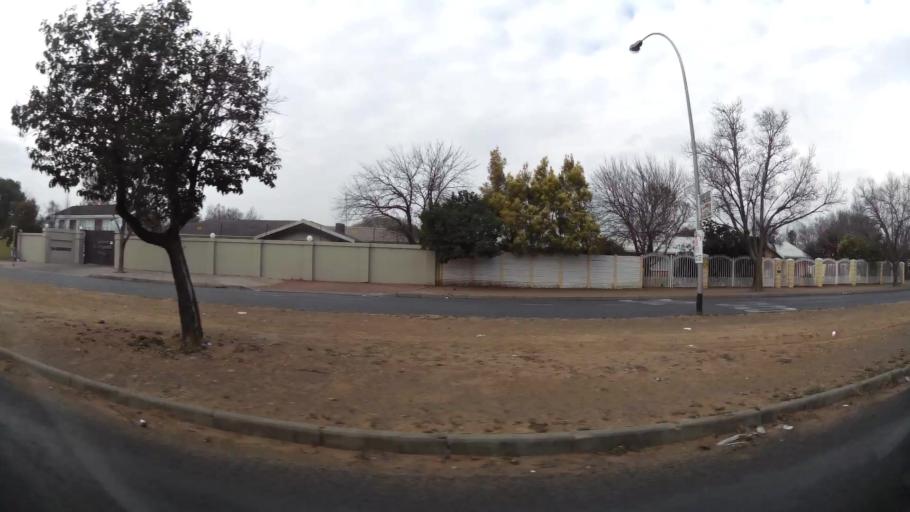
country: ZA
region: Orange Free State
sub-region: Mangaung Metropolitan Municipality
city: Bloemfontein
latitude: -29.1189
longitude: 26.1802
